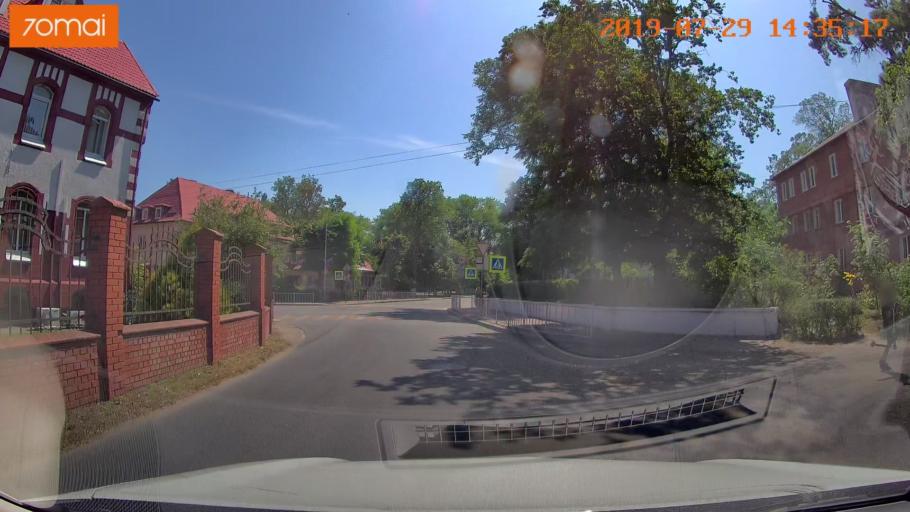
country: RU
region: Kaliningrad
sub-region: Gorod Kaliningrad
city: Baltiysk
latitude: 54.6444
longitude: 19.8921
